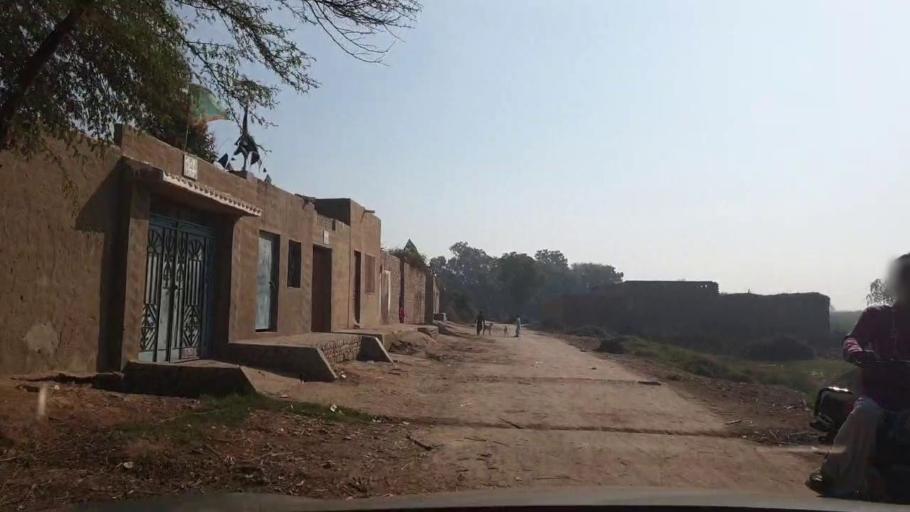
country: PK
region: Sindh
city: Tando Allahyar
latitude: 25.5921
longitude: 68.7185
